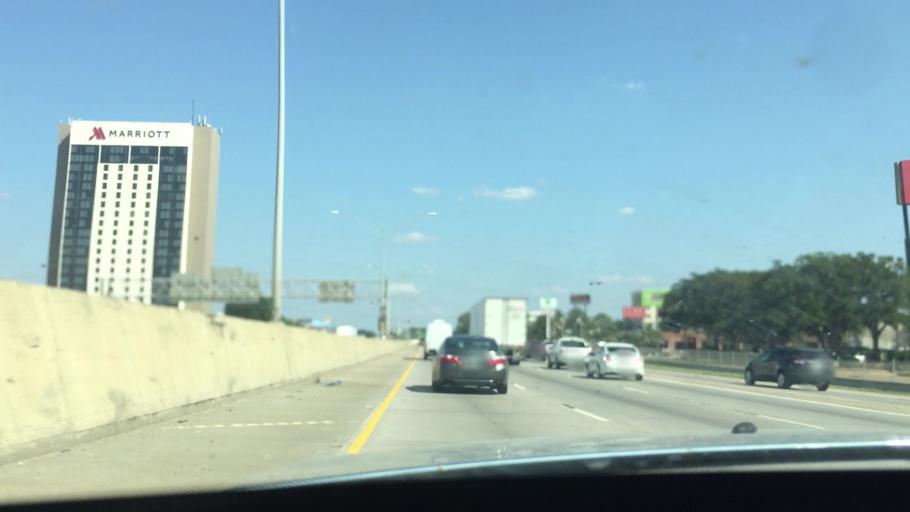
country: US
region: Louisiana
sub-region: East Baton Rouge Parish
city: Baton Rouge
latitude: 30.4227
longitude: -91.1373
